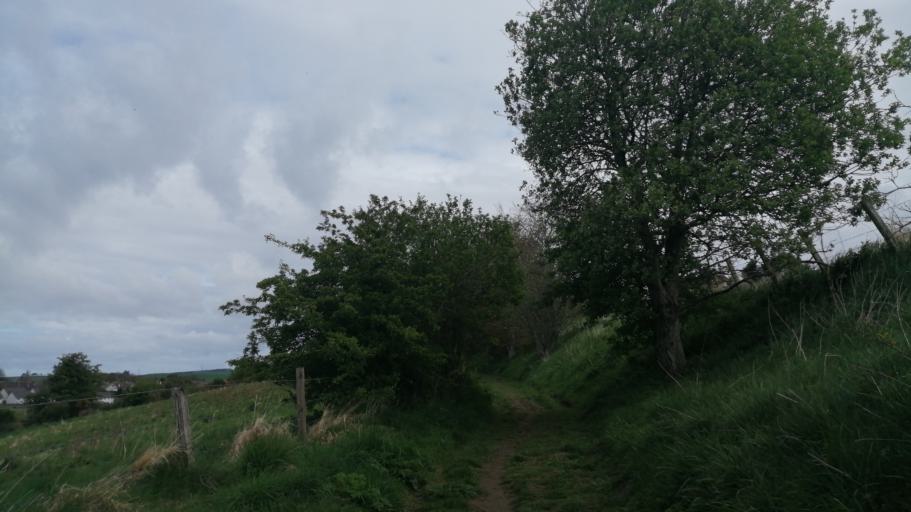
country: GB
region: Scotland
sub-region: Moray
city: Keith
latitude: 57.5349
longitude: -2.9603
